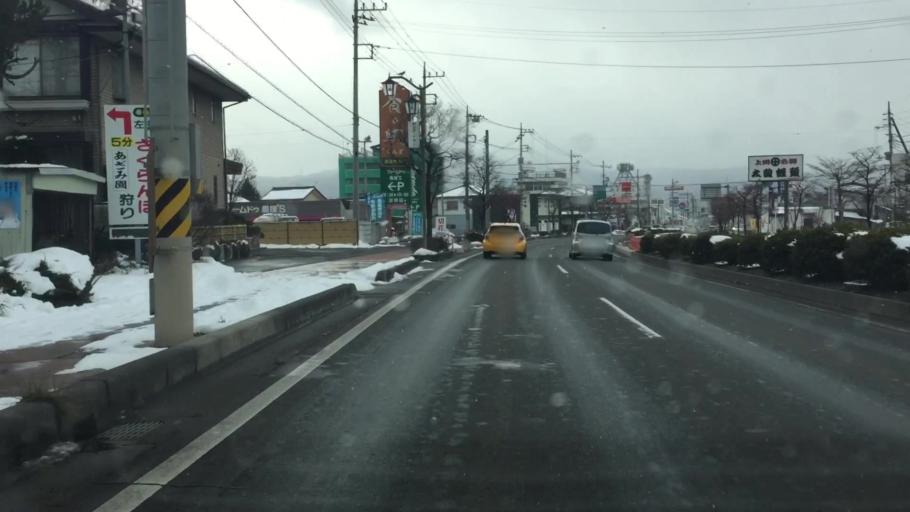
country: JP
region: Gunma
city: Numata
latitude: 36.6556
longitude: 139.0747
